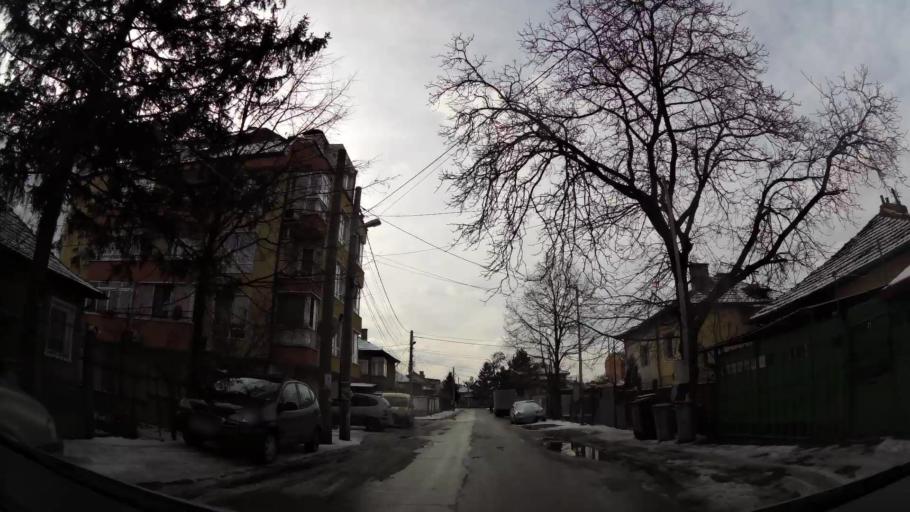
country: BG
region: Sofia-Capital
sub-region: Stolichna Obshtina
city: Sofia
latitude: 42.7010
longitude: 23.3824
